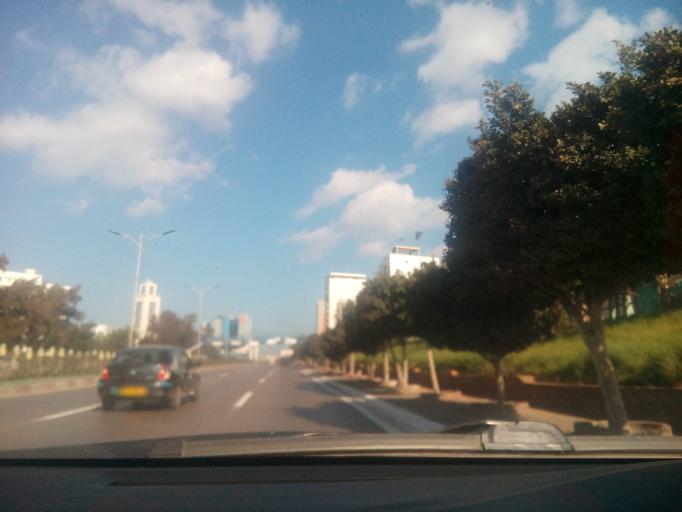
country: DZ
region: Oran
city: Oran
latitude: 35.6923
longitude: -0.6064
